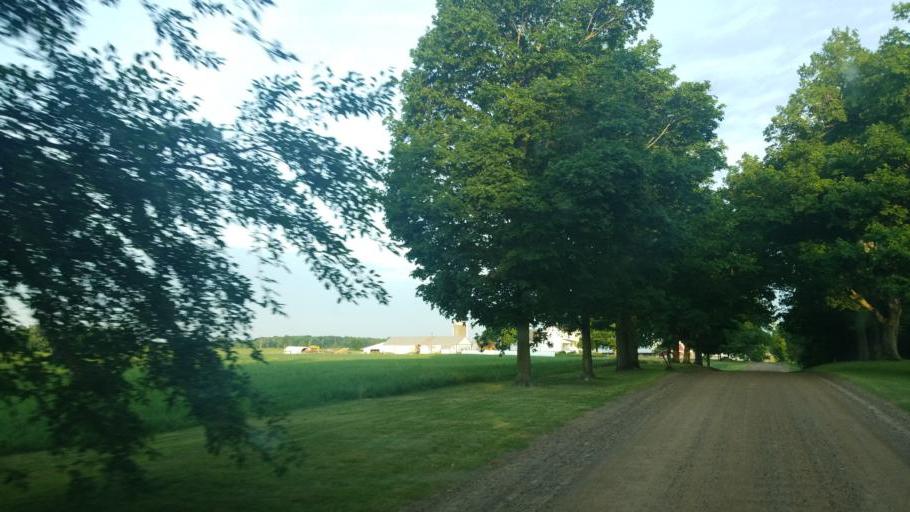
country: US
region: Michigan
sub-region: Barry County
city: Nashville
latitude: 42.5969
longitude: -84.9872
